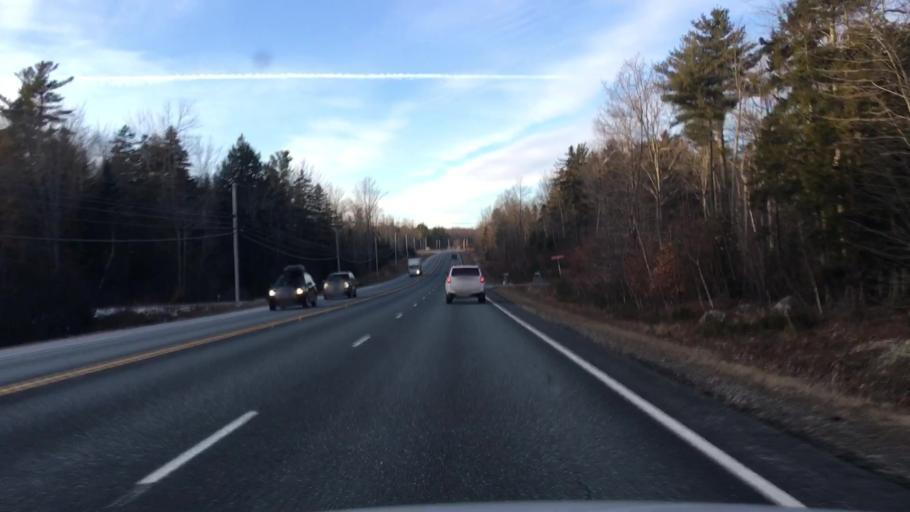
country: US
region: Maine
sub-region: Hancock County
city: Dedham
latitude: 44.6391
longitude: -68.5502
